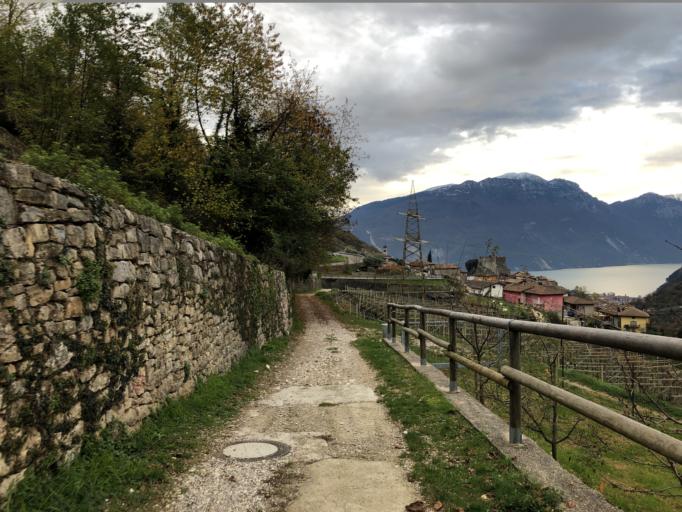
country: IT
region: Trentino-Alto Adige
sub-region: Provincia di Trento
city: Tenno
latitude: 45.9237
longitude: 10.8289
